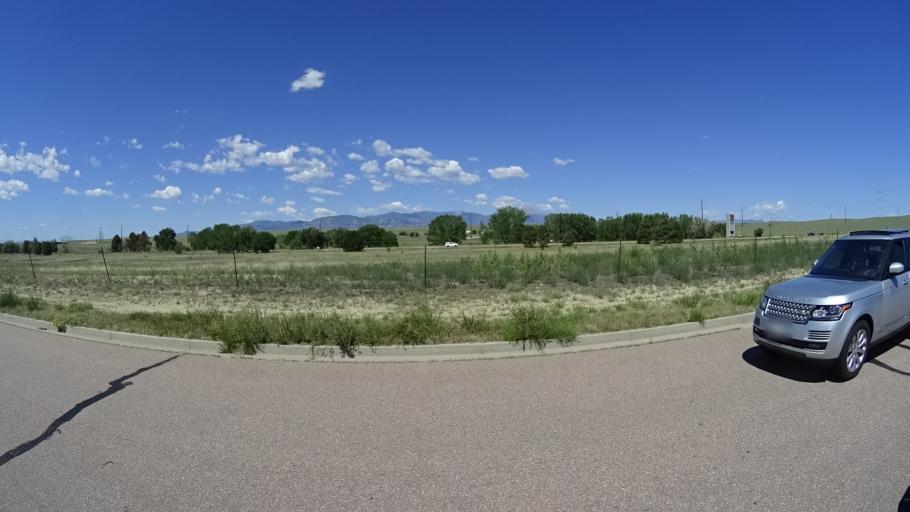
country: US
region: Colorado
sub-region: El Paso County
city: Security-Widefield
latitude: 38.7790
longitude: -104.6575
